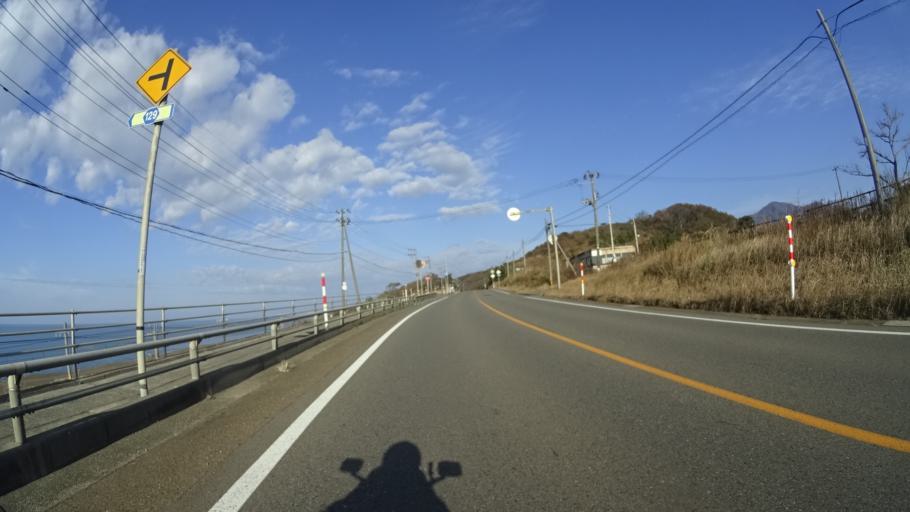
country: JP
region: Niigata
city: Kashiwazaki
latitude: 37.2915
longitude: 138.4019
